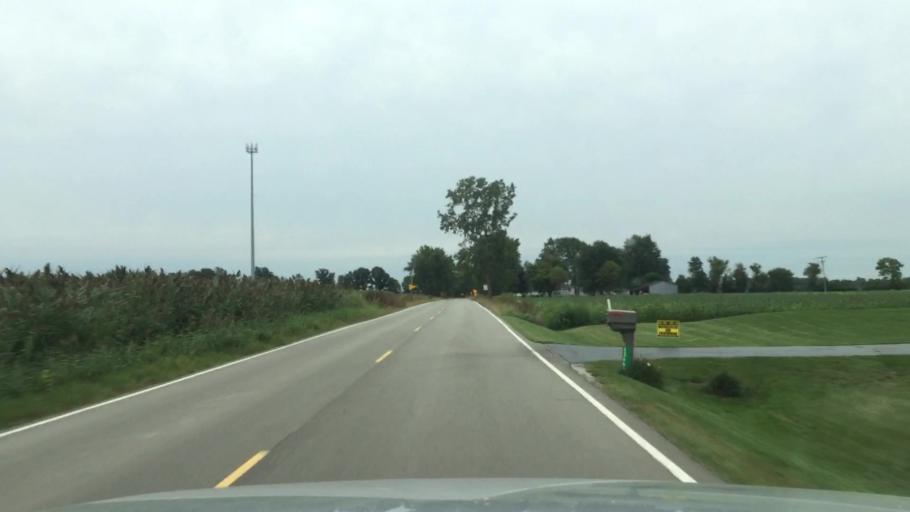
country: US
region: Michigan
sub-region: Washtenaw County
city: Milan
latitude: 42.0885
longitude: -83.7352
